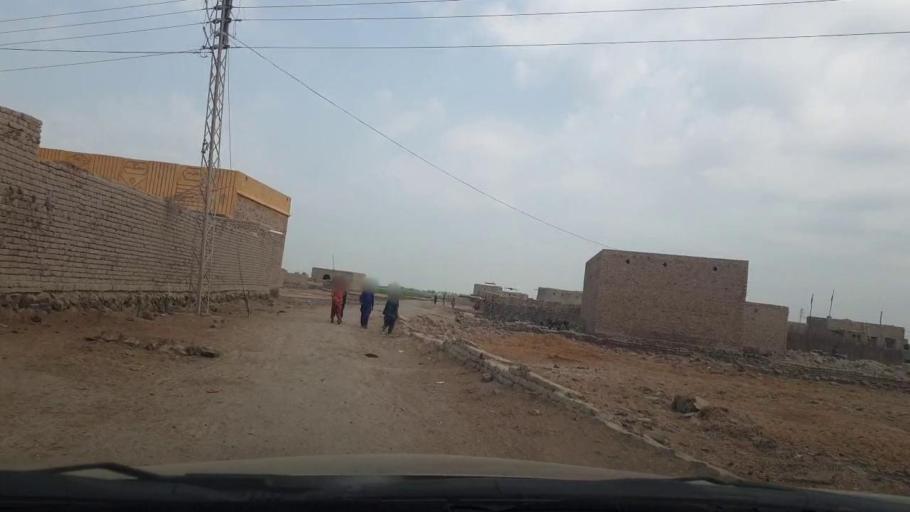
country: PK
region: Sindh
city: Ratodero
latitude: 27.7023
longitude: 68.2295
